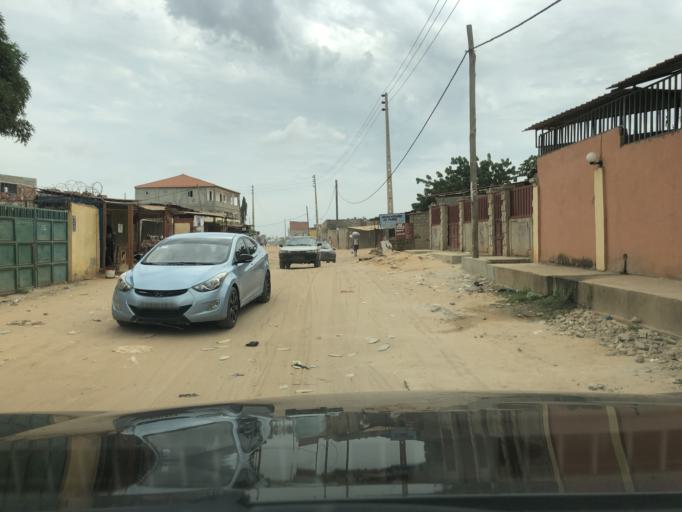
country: AO
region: Luanda
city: Luanda
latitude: -8.9313
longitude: 13.2322
